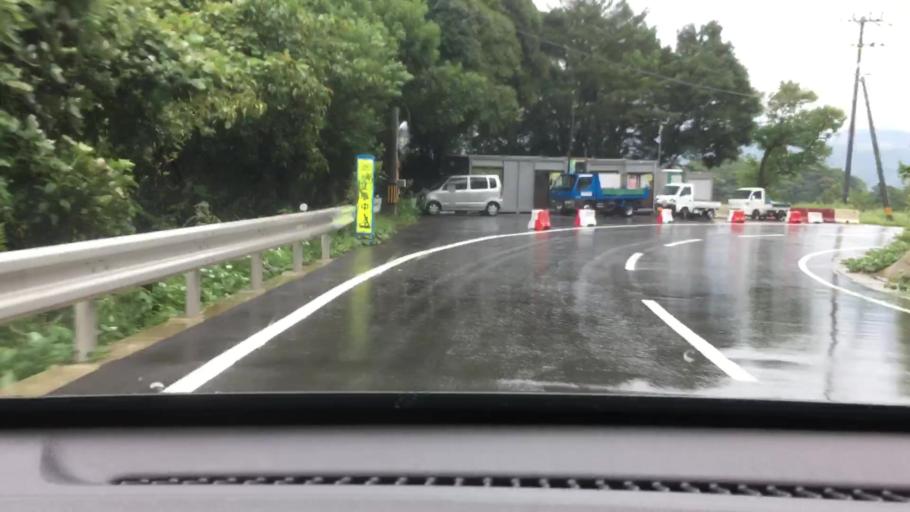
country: JP
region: Nagasaki
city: Togitsu
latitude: 32.8701
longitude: 129.7663
